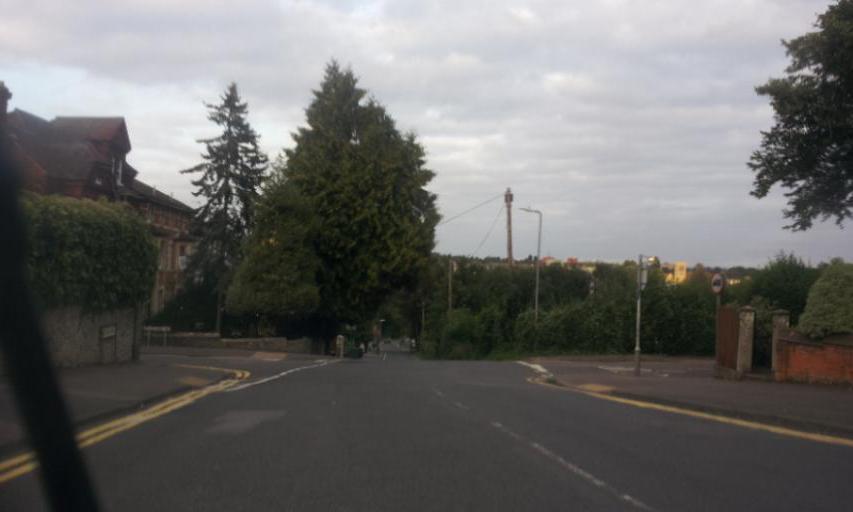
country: GB
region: England
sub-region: Kent
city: Maidstone
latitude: 51.2768
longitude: 0.5115
